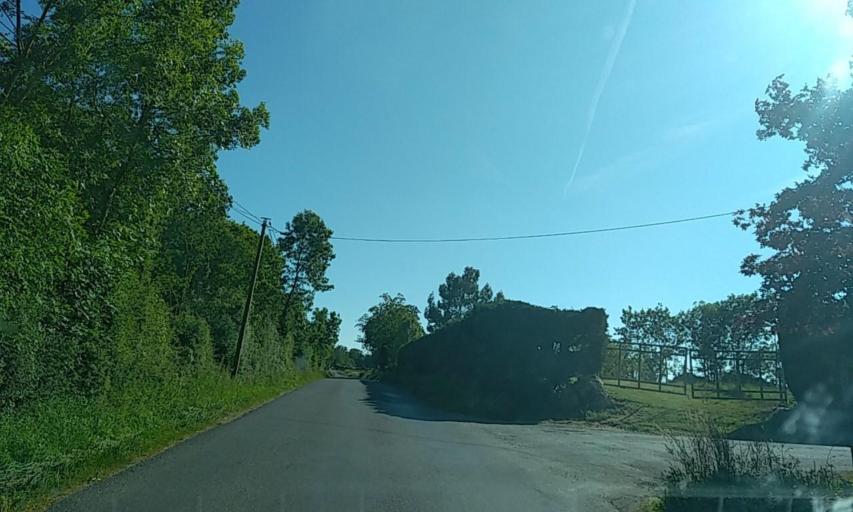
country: FR
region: Poitou-Charentes
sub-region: Departement des Deux-Sevres
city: Boisme
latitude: 46.7946
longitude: -0.4270
